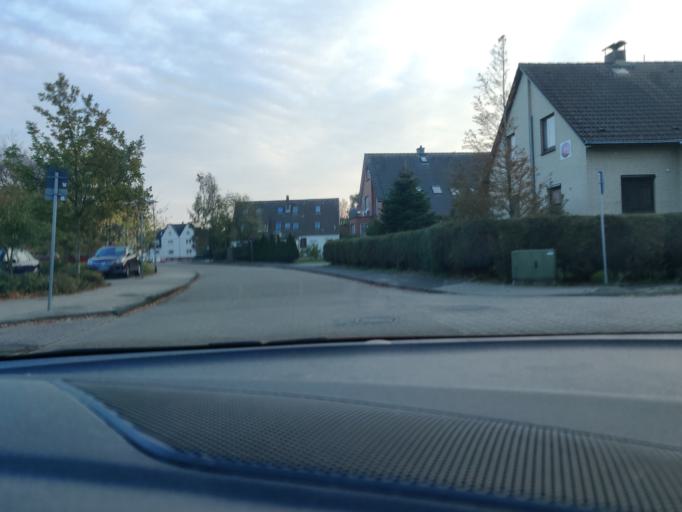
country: DE
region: Lower Saxony
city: Cuxhaven
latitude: 53.8877
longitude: 8.6608
